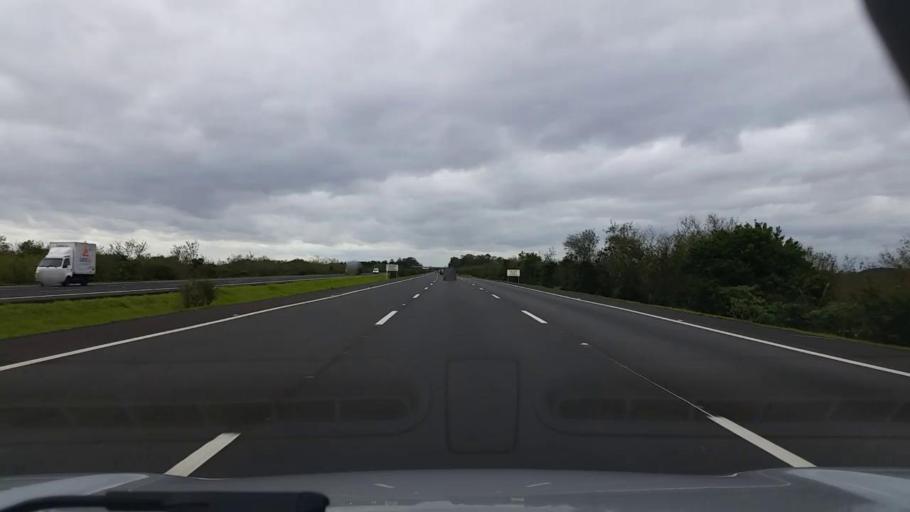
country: BR
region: Rio Grande do Sul
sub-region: Rolante
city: Rolante
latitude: -29.8840
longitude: -50.5672
